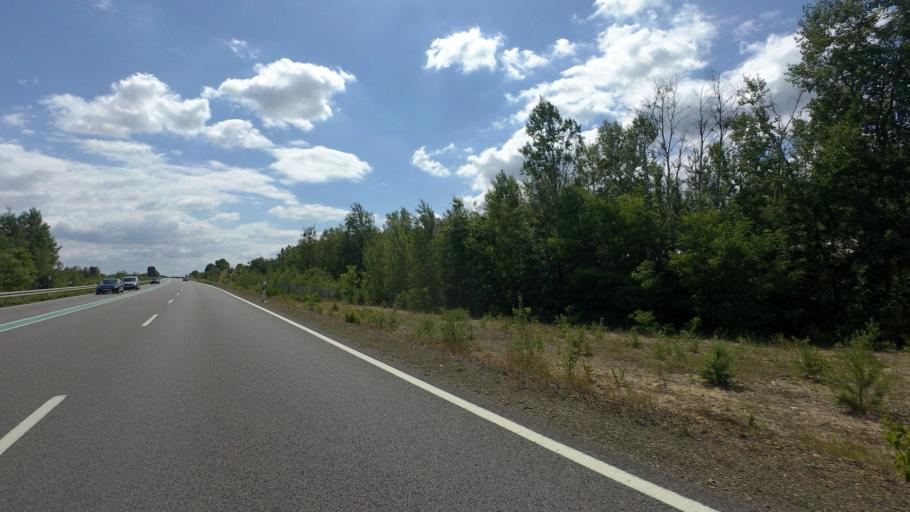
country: DE
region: Brandenburg
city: Senftenberg
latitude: 51.5235
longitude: 13.9644
